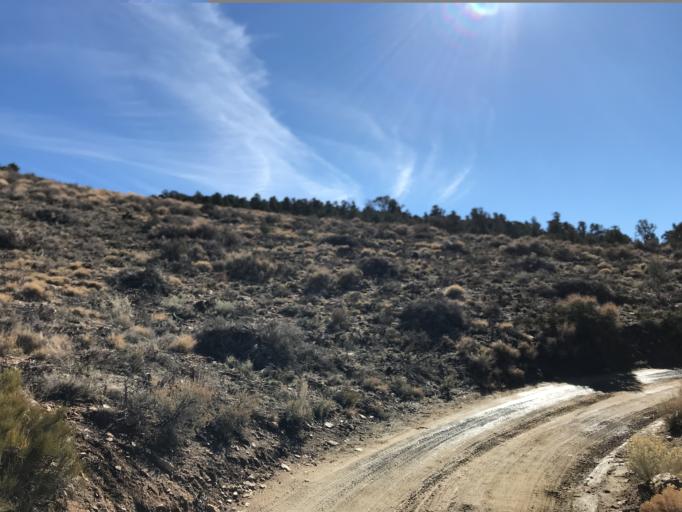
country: US
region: California
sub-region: San Bernardino County
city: Big Bear City
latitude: 34.2777
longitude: -116.7846
